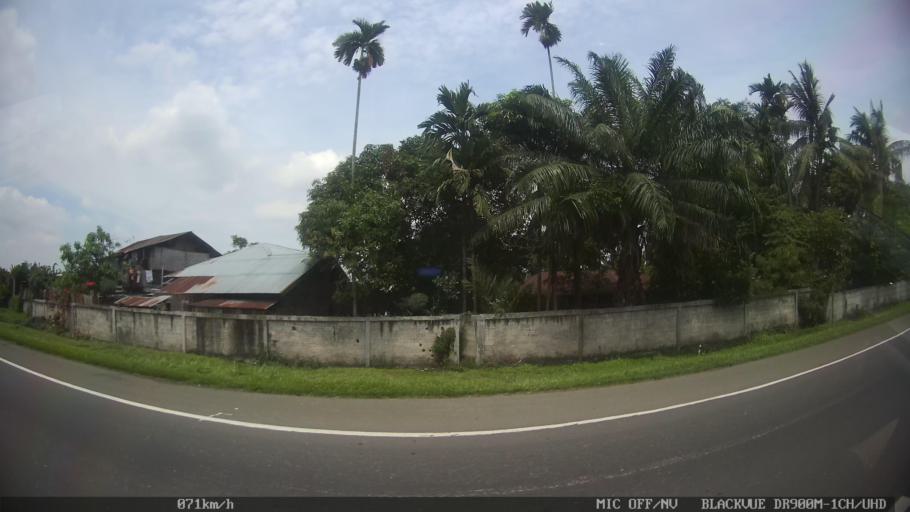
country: ID
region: North Sumatra
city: Labuhan Deli
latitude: 3.6945
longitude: 98.6817
